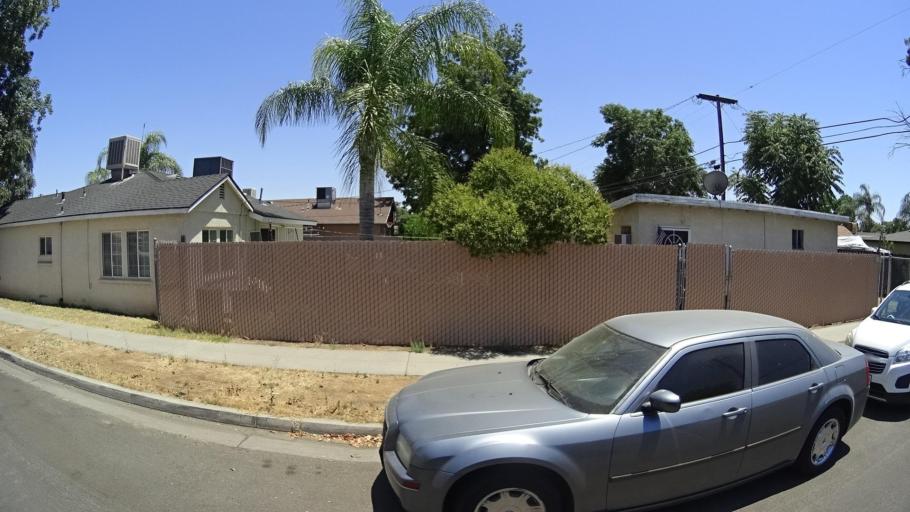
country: US
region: California
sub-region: Fresno County
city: Fresno
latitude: 36.7329
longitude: -119.7410
